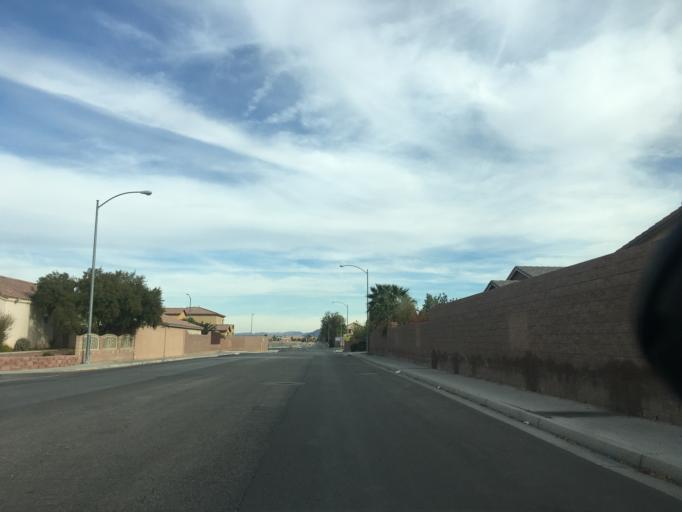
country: US
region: Nevada
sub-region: Clark County
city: Enterprise
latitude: 36.0172
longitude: -115.1654
